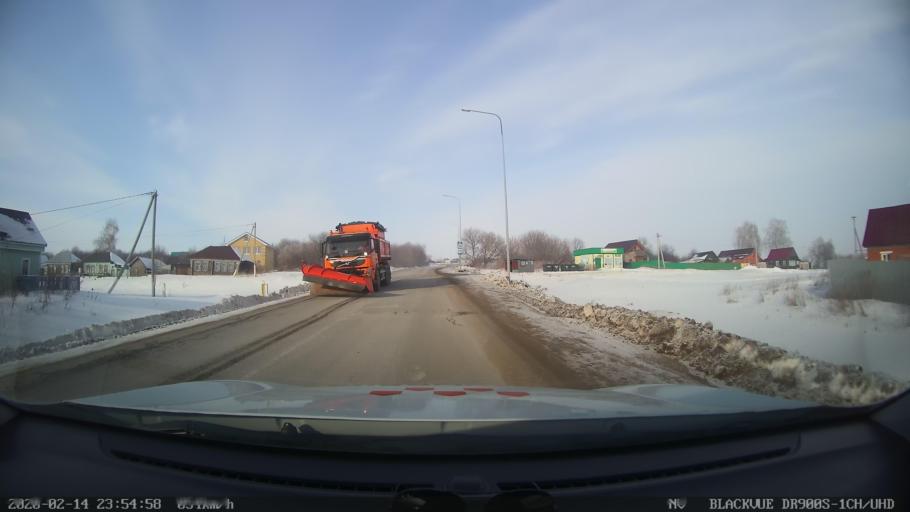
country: RU
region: Tatarstan
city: Kuybyshevskiy Zaton
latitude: 55.3132
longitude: 49.1447
